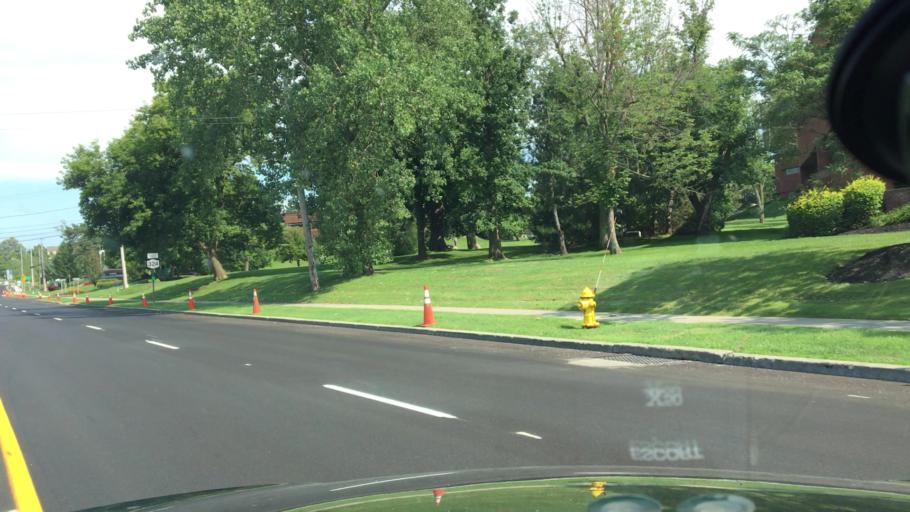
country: US
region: New York
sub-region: Erie County
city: Harris Hill
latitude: 42.9781
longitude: -78.7022
